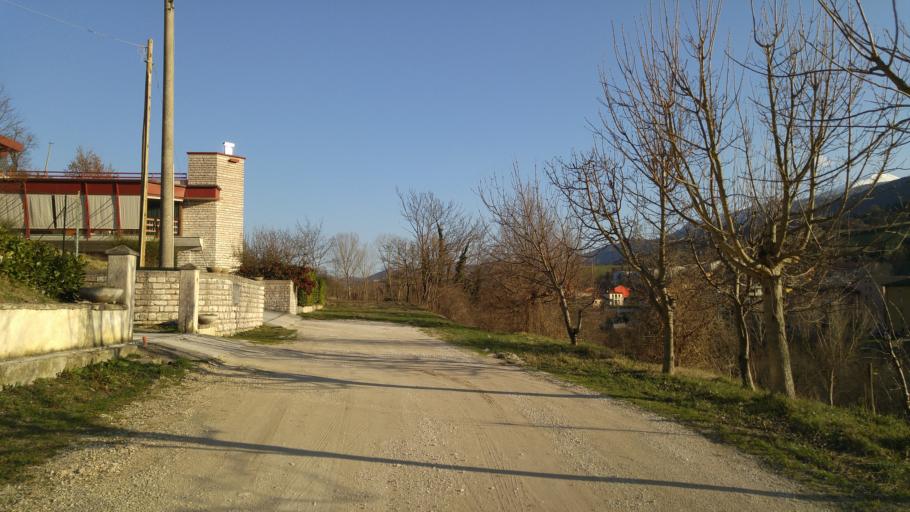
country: IT
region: The Marches
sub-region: Provincia di Pesaro e Urbino
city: Cagli
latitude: 43.5480
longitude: 12.6606
